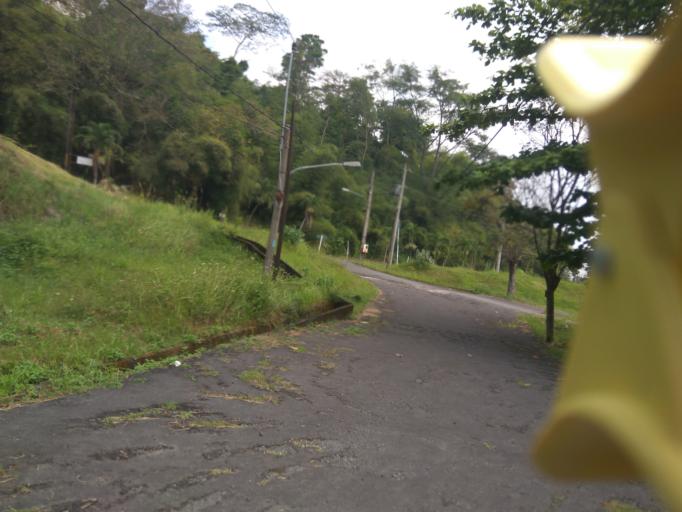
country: ID
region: Central Java
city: Semarang
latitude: -7.0424
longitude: 110.4162
